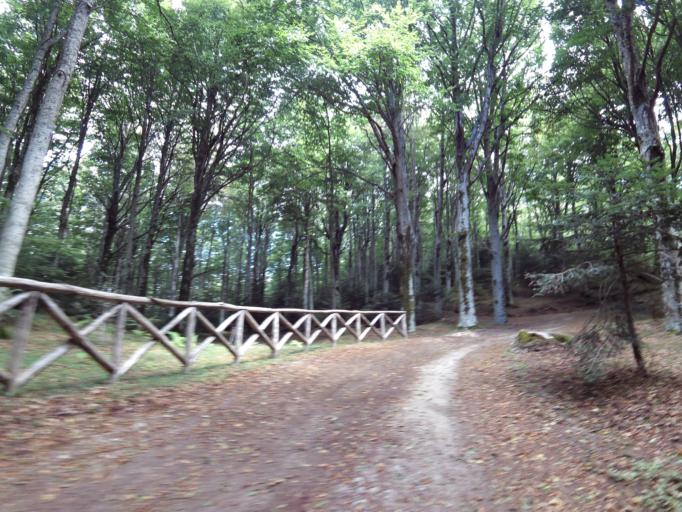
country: IT
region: Calabria
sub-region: Provincia di Vibo-Valentia
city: Mongiana
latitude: 38.5210
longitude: 16.3446
